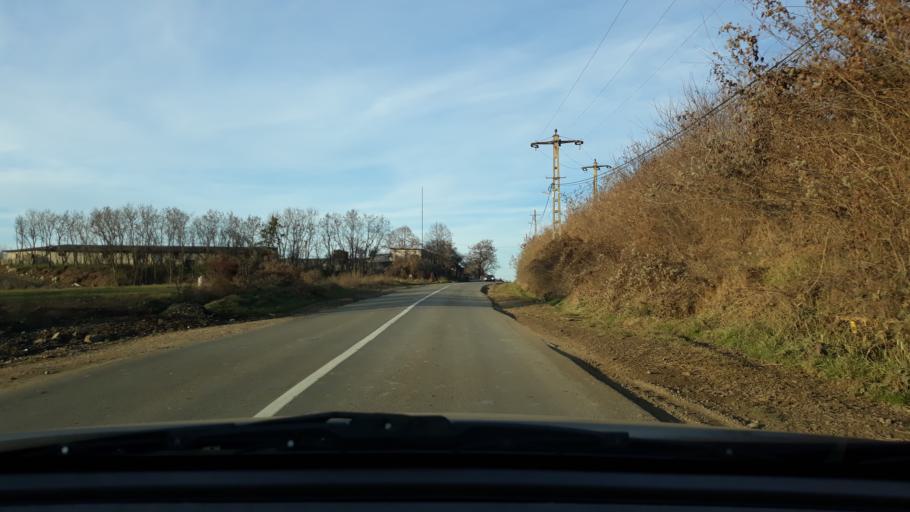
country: RO
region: Bihor
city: Foglas
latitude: 47.2467
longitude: 22.5335
